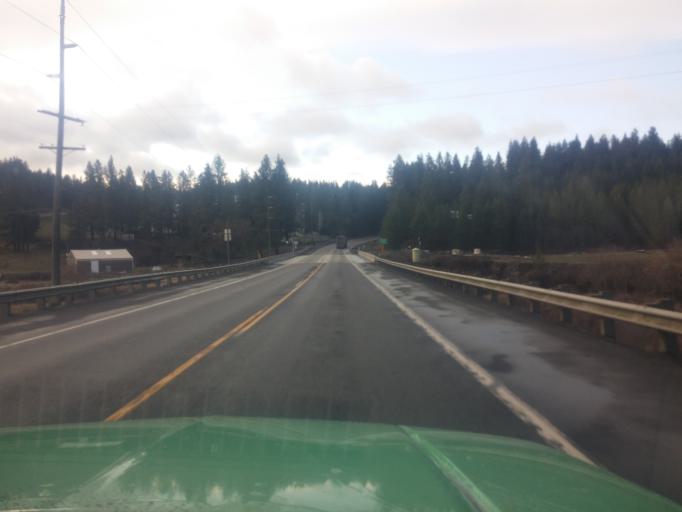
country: US
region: Idaho
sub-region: Latah County
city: Moscow
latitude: 46.9163
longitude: -116.9516
